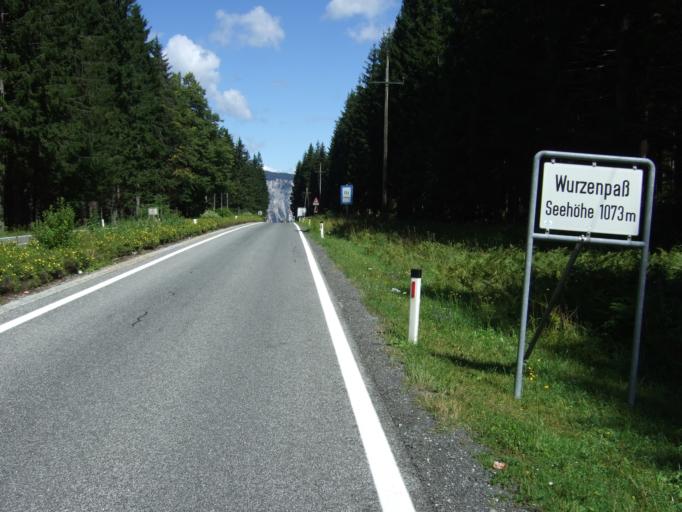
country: AT
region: Carinthia
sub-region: Politischer Bezirk Villach Land
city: Arnoldstein
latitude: 46.5227
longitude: 13.7519
